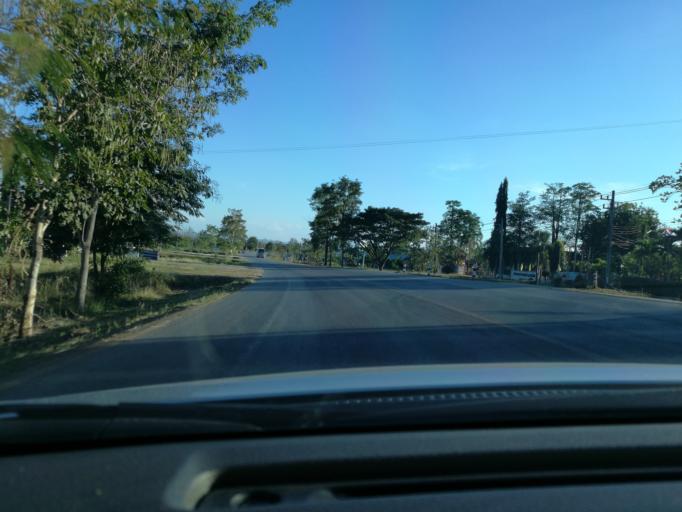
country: TH
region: Phitsanulok
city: Nakhon Thai
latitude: 17.0571
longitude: 100.8098
